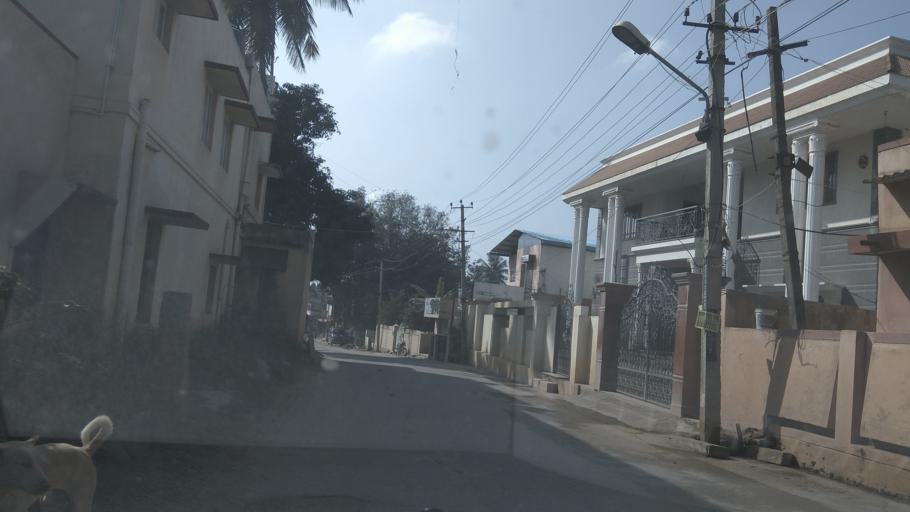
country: IN
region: Karnataka
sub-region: Bangalore Urban
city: Bangalore
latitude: 12.9482
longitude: 77.6807
